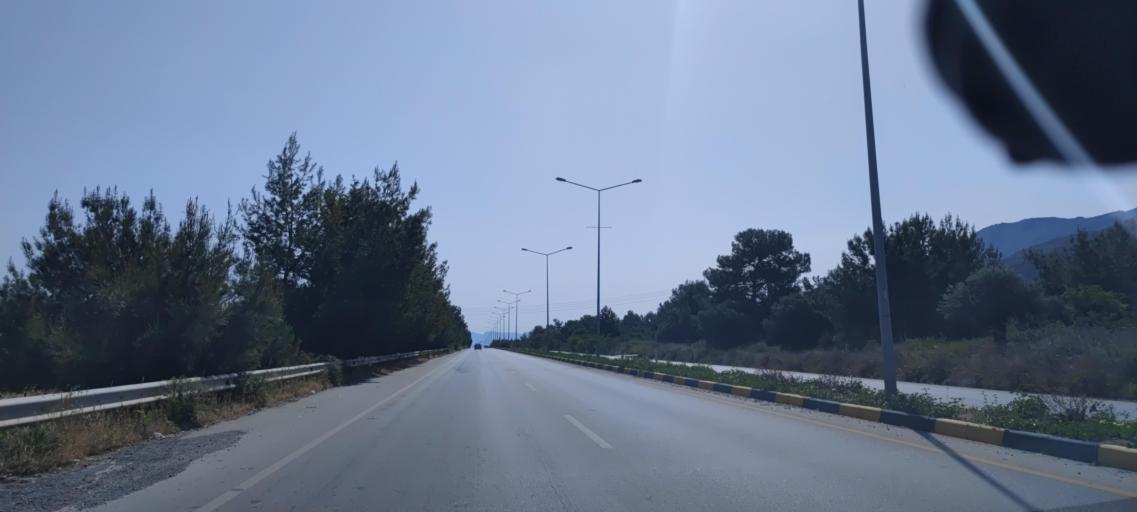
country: CY
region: Keryneia
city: Kyrenia
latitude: 35.3287
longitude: 33.2891
